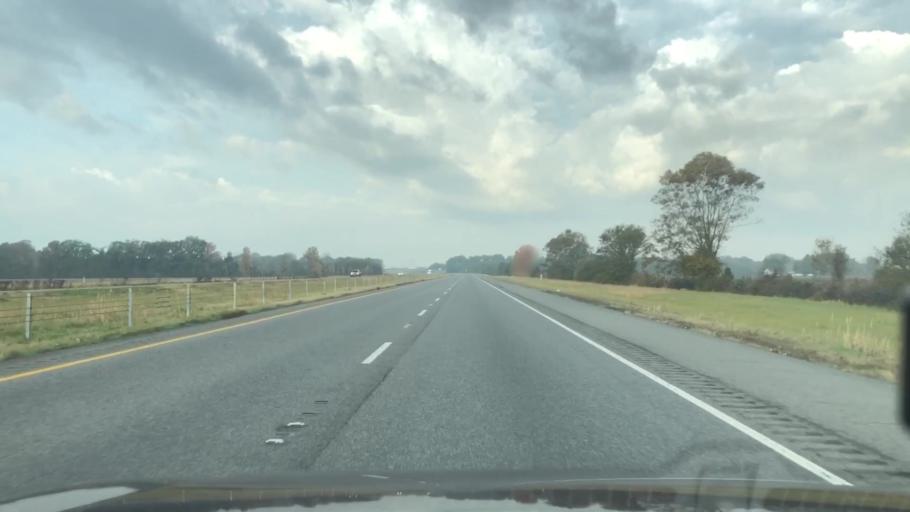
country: US
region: Louisiana
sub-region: Madison Parish
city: Tallulah
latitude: 32.4181
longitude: -91.2867
